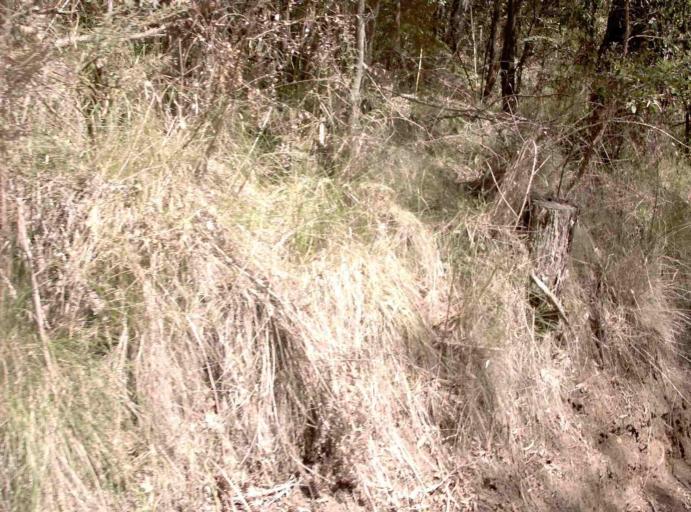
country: AU
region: Victoria
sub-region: East Gippsland
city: Lakes Entrance
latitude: -37.2238
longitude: 148.2635
